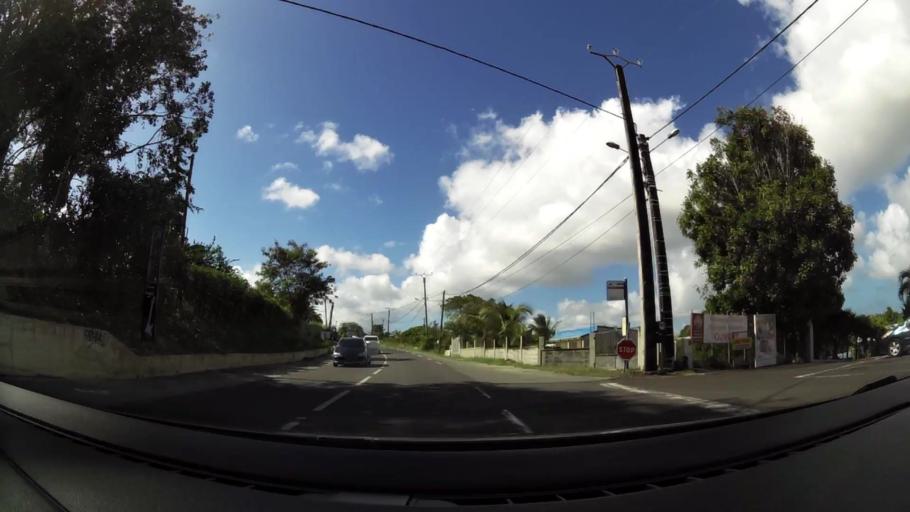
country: GP
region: Guadeloupe
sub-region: Guadeloupe
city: Sainte-Anne
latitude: 16.2523
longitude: -61.3519
